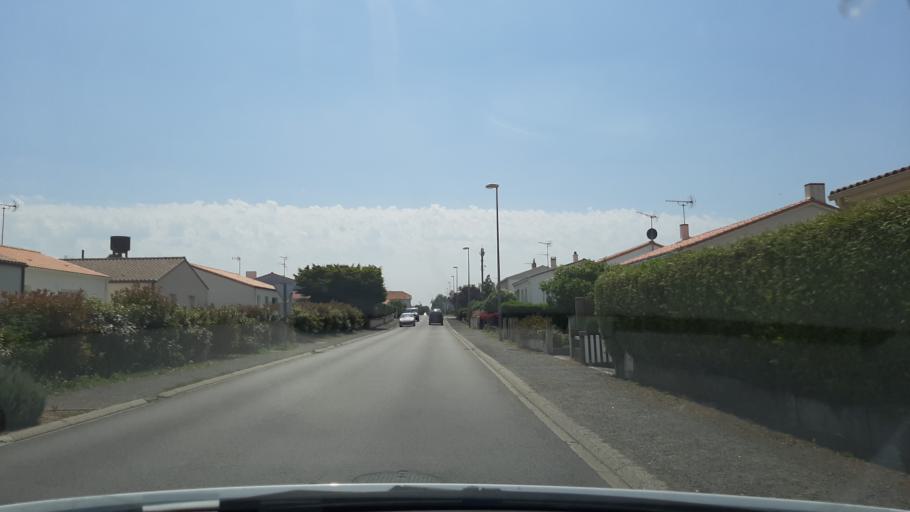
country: FR
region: Pays de la Loire
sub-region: Departement de la Vendee
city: Le Poire-sur-Vie
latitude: 46.7728
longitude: -1.5092
